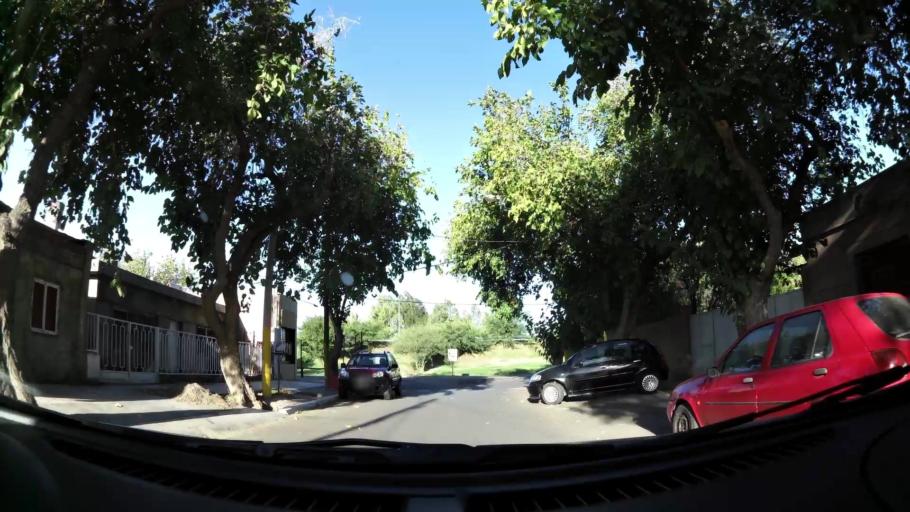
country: AR
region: San Juan
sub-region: Departamento de Santa Lucia
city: Santa Lucia
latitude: -31.5368
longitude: -68.5046
